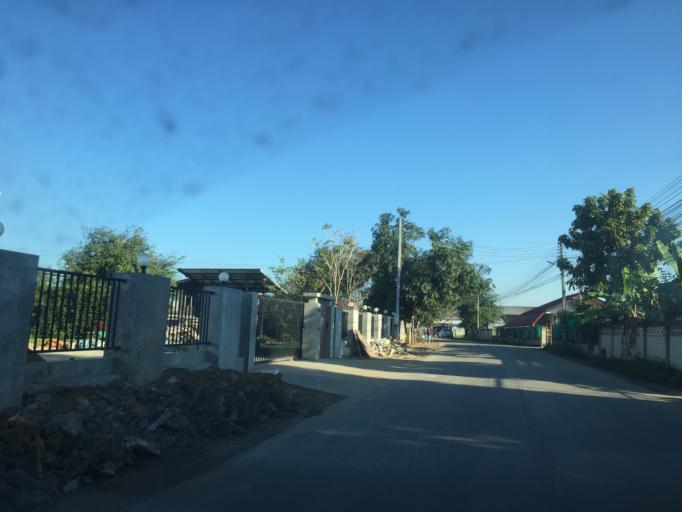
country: TH
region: Lamphun
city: Lamphun
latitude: 18.6091
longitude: 99.0563
